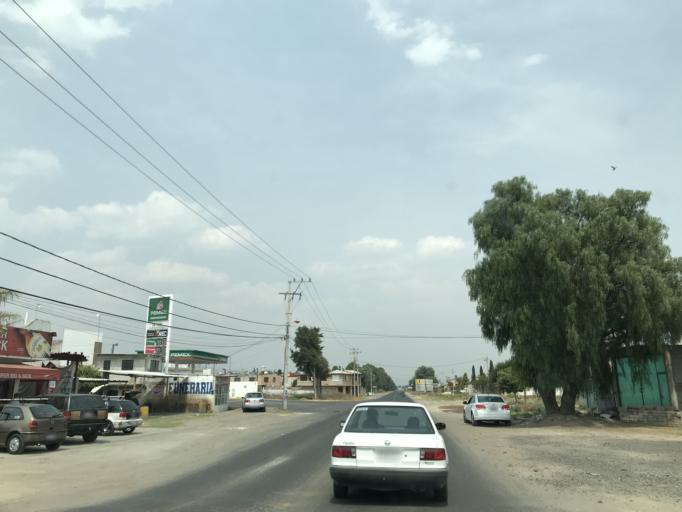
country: MX
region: Tlaxcala
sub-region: Ixtacuixtla de Mariano Matamoros
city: Santa Justina Ecatepec
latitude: 19.3078
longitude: -98.3706
